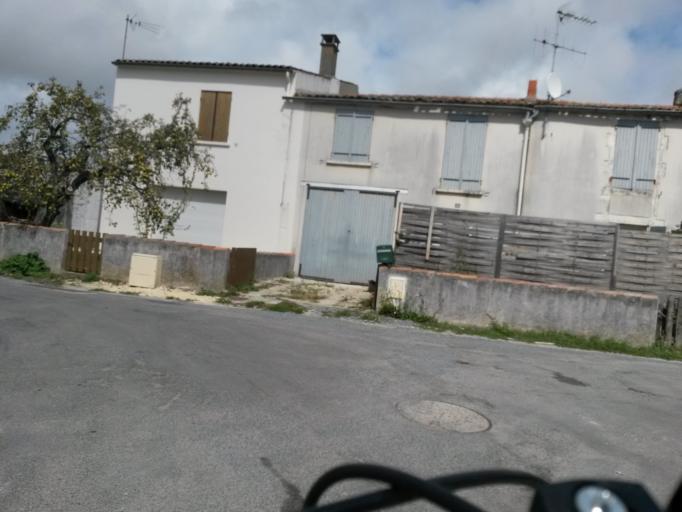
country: FR
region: Poitou-Charentes
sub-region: Departement de la Charente-Maritime
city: Dolus-d'Oleron
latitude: 45.9439
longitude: -1.2884
